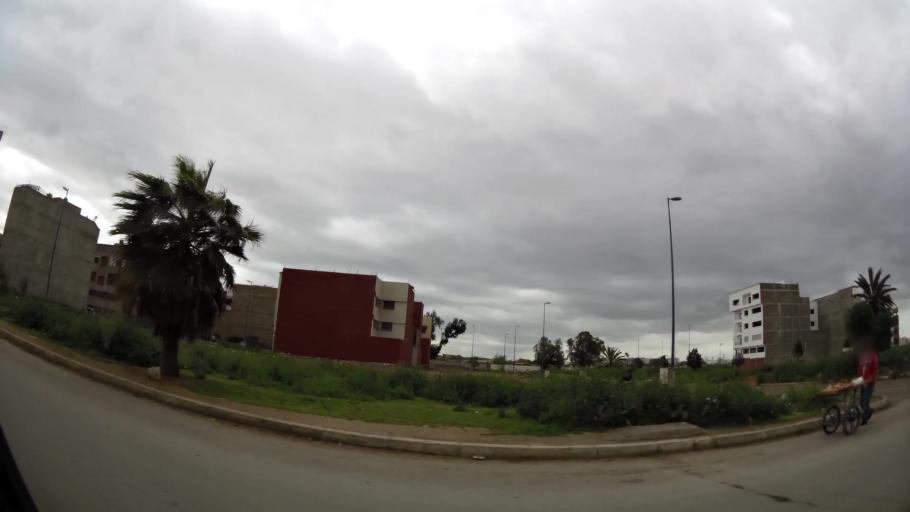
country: MA
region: Grand Casablanca
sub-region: Mediouna
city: Tit Mellil
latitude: 33.5541
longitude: -7.5340
